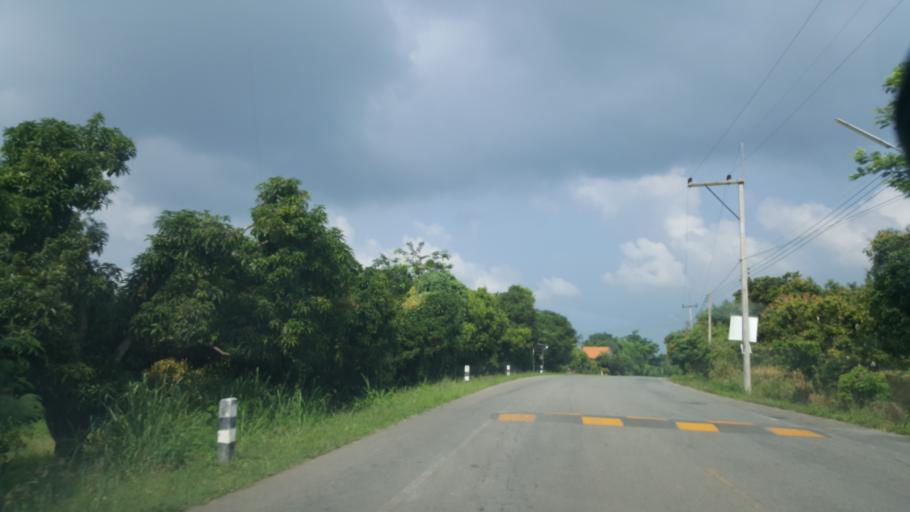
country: TH
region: Chon Buri
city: Sattahip
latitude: 12.7161
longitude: 100.9203
